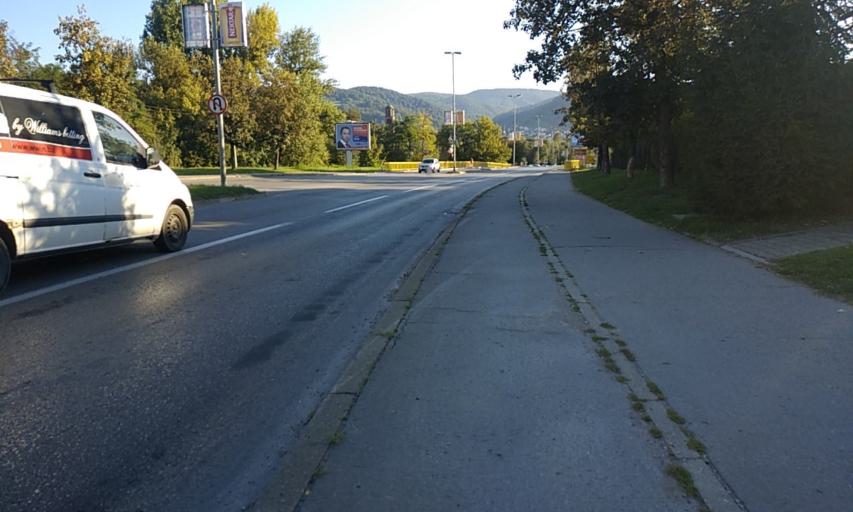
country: BA
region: Republika Srpska
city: Starcevica
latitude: 44.7688
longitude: 17.2101
